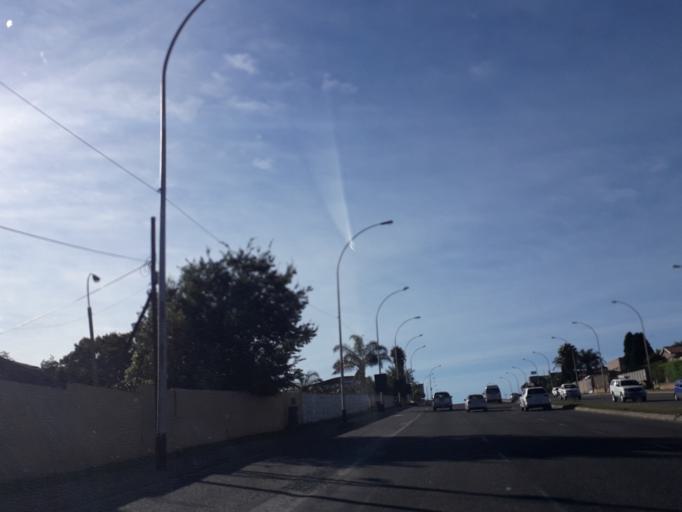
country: ZA
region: Gauteng
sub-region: City of Johannesburg Metropolitan Municipality
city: Roodepoort
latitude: -26.1646
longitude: 27.9361
